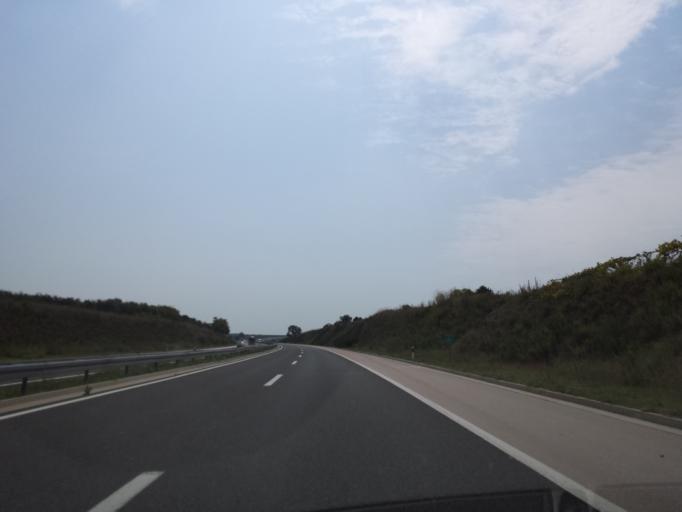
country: HR
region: Zadarska
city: Policnik
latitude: 44.1610
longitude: 15.4191
